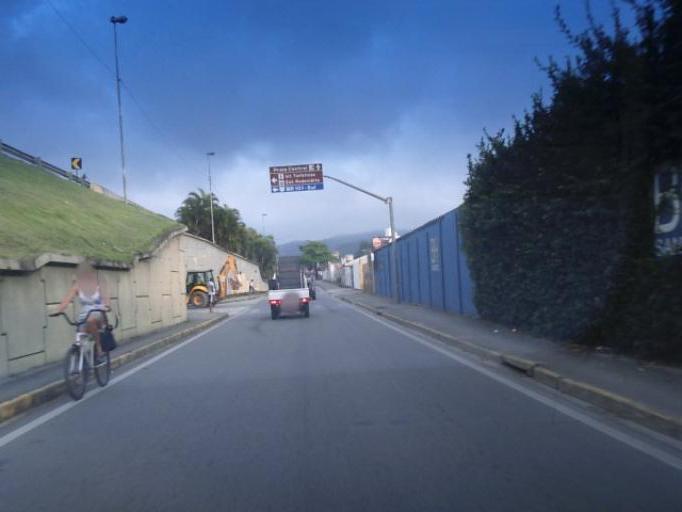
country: BR
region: Santa Catarina
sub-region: Itapema
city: Itapema
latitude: -27.1065
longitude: -48.6143
